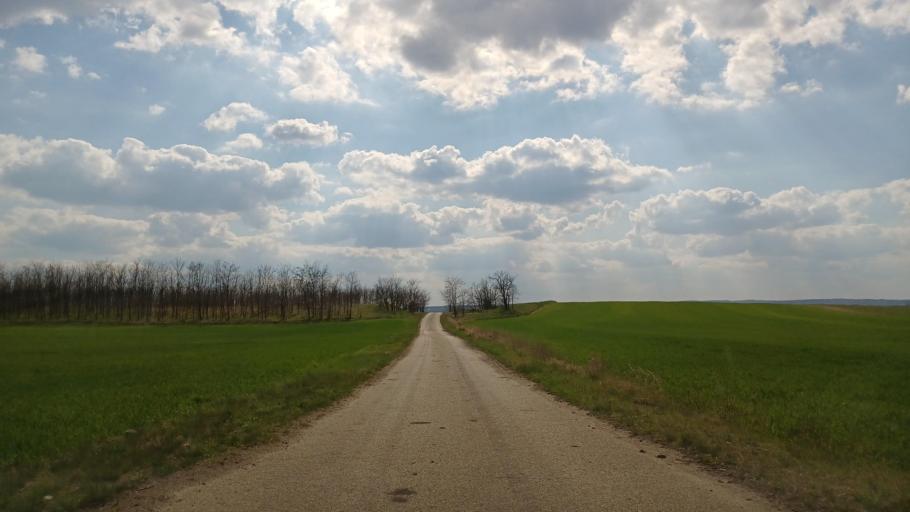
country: HU
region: Fejer
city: Cece
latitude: 46.7403
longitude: 18.6390
